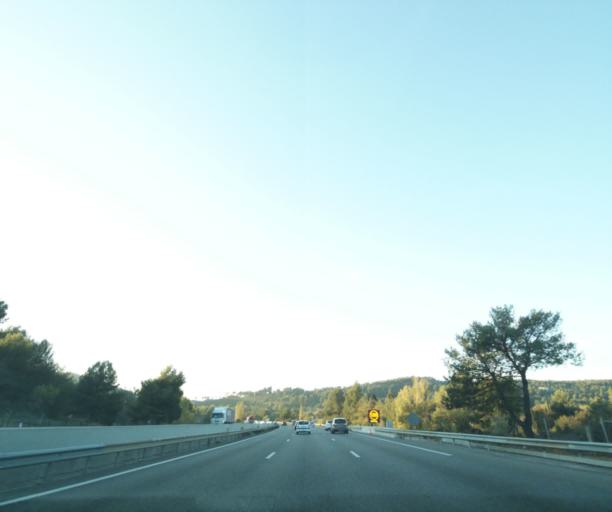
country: FR
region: Provence-Alpes-Cote d'Azur
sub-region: Departement des Bouches-du-Rhone
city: Le Tholonet
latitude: 43.5012
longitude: 5.5209
